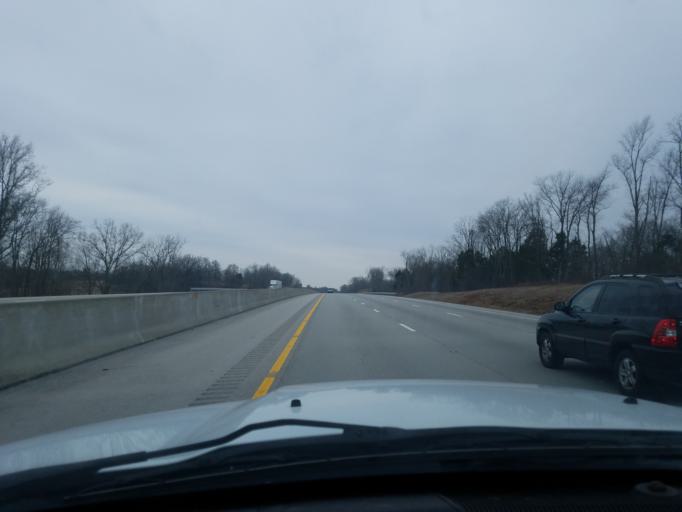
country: US
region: Kentucky
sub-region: Barren County
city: Cave City
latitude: 37.0740
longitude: -86.0845
